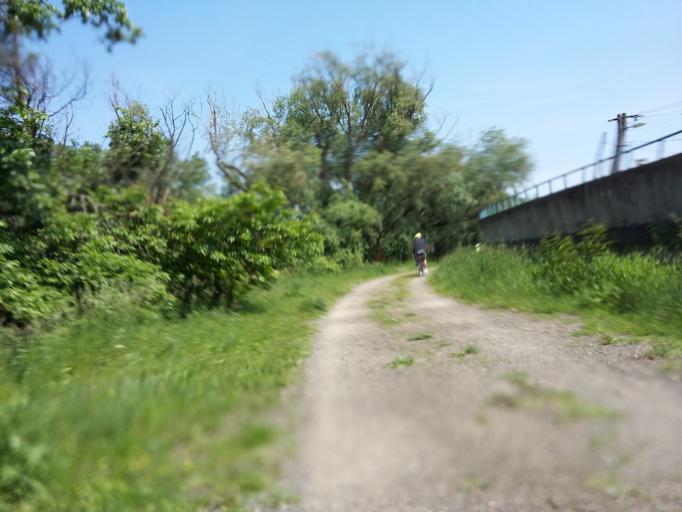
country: AT
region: Lower Austria
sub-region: Politischer Bezirk Ganserndorf
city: Angern an der March
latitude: 48.4074
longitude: 16.8530
